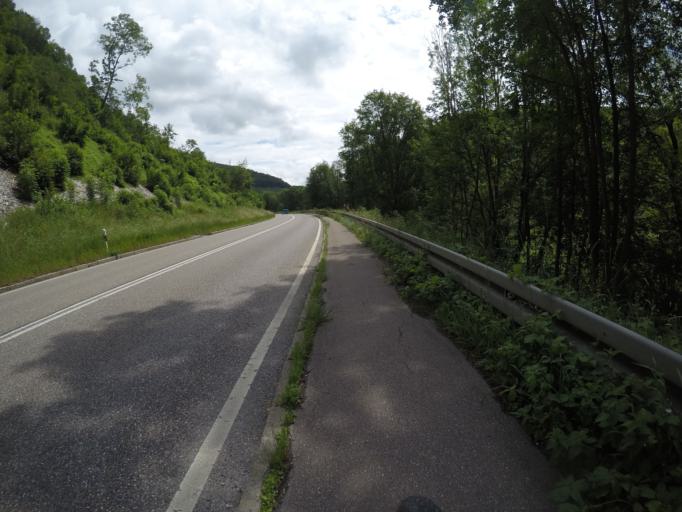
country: DE
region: Baden-Wuerttemberg
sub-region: Regierungsbezirk Stuttgart
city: Geislingen an der Steige
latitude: 48.5991
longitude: 9.8432
